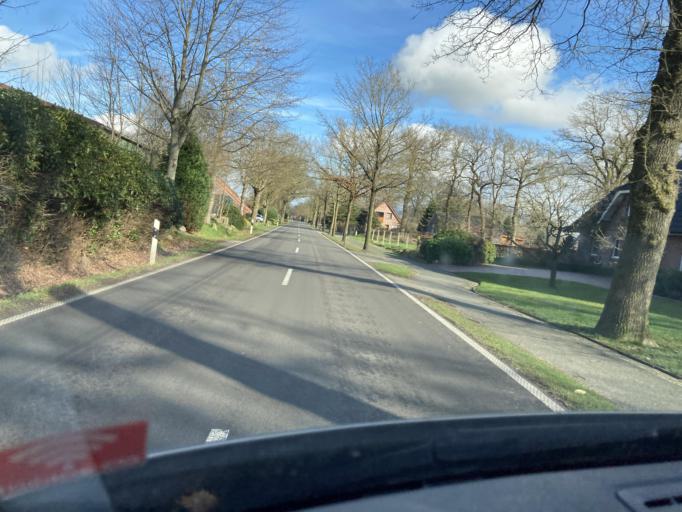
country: DE
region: Lower Saxony
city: Schwerinsdorf
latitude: 53.2798
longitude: 7.7217
